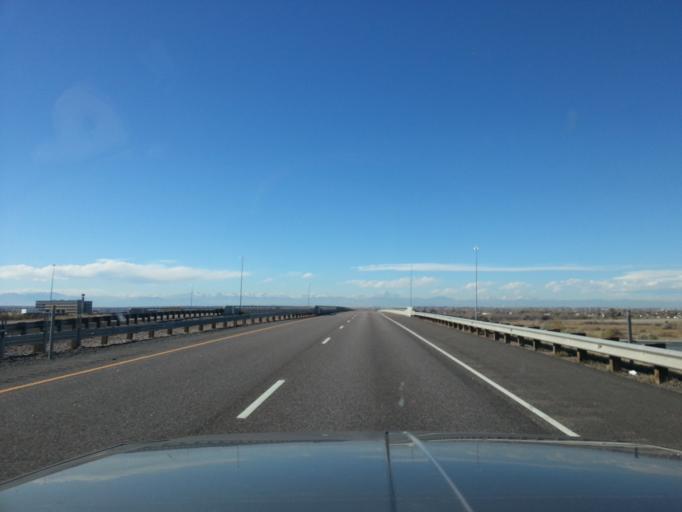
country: US
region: Colorado
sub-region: Adams County
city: Brighton
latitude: 39.9241
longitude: -104.8012
